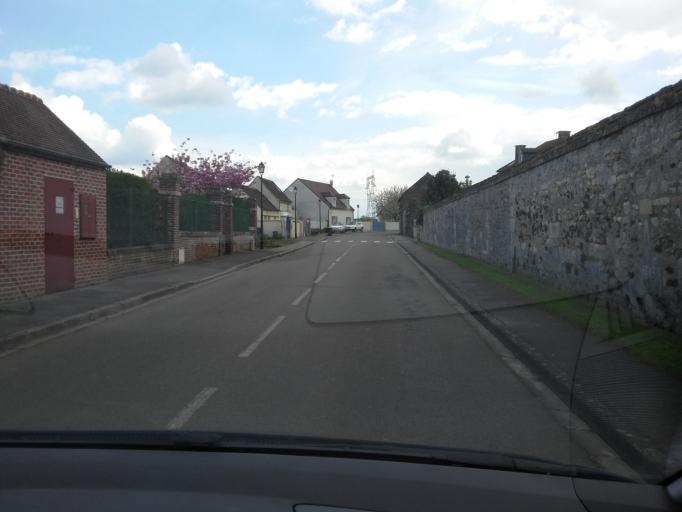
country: FR
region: Picardie
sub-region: Departement de l'Oise
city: Longueil-Sainte-Marie
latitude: 49.3719
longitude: 2.6988
